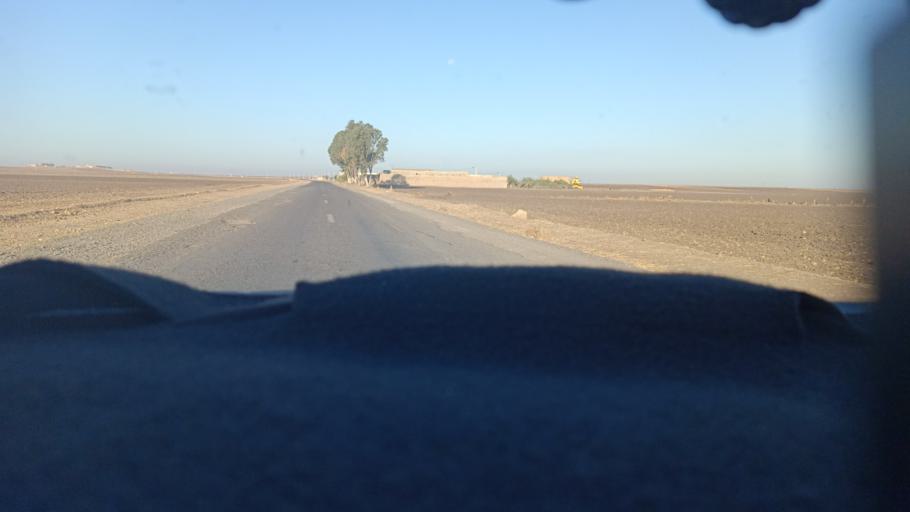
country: MA
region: Doukkala-Abda
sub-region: Safi
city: Youssoufia
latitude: 32.3714
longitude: -8.7147
